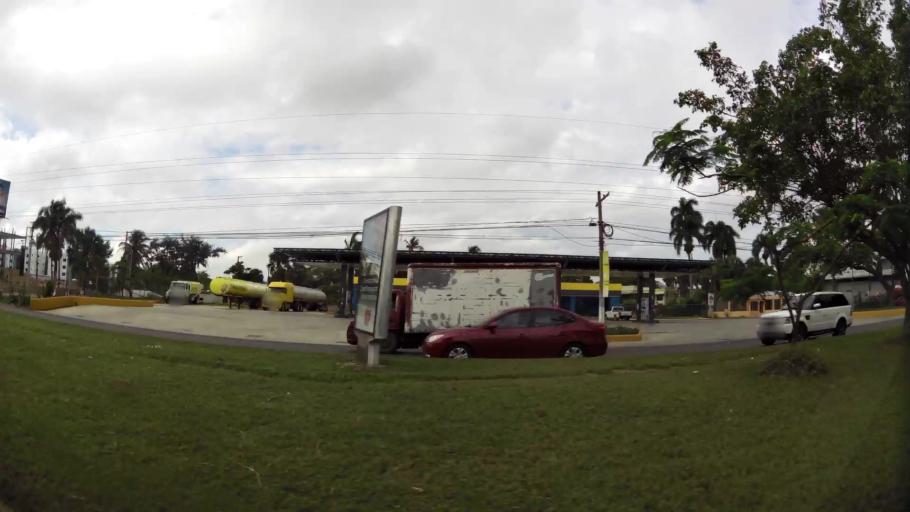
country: DO
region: Santiago
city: Licey al Medio
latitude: 19.4223
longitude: -70.6496
